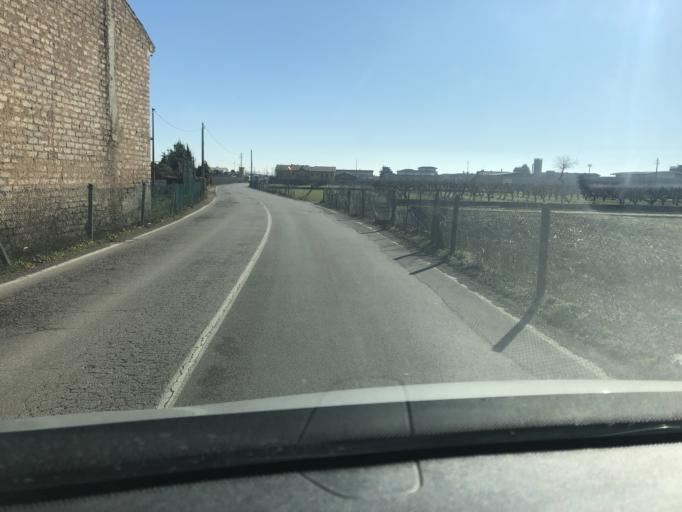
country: IT
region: Veneto
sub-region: Provincia di Verona
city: Lugagnano
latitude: 45.4358
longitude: 10.8683
